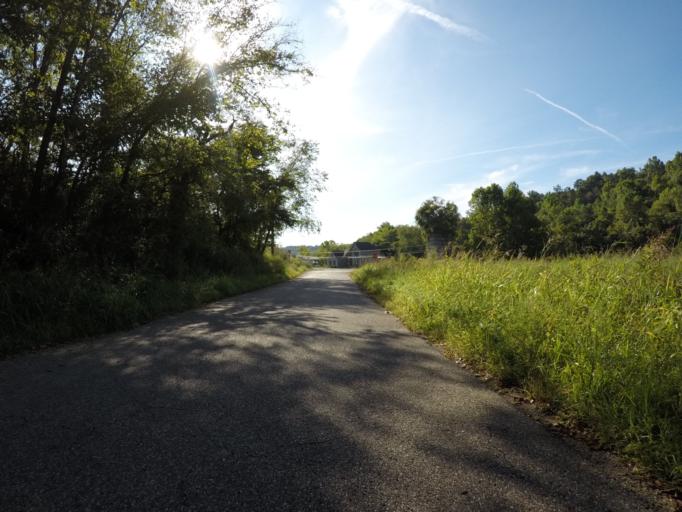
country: US
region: Ohio
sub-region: Lawrence County
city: Burlington
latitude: 38.4993
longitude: -82.5106
